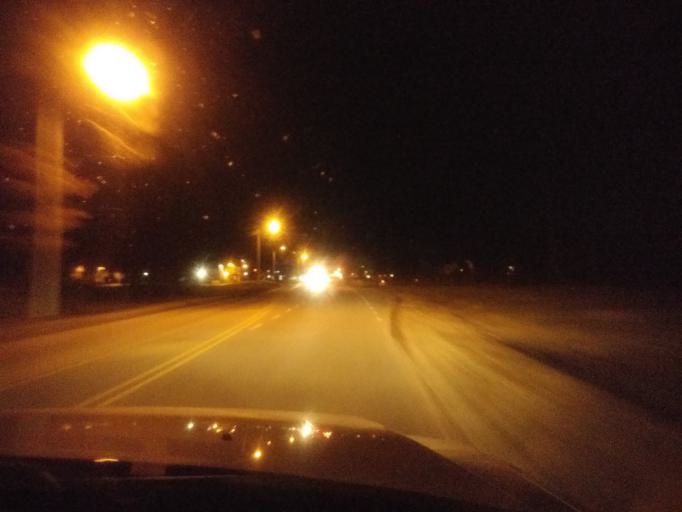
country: US
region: Virginia
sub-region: City of Chesapeake
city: Chesapeake
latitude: 36.7862
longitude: -76.1951
